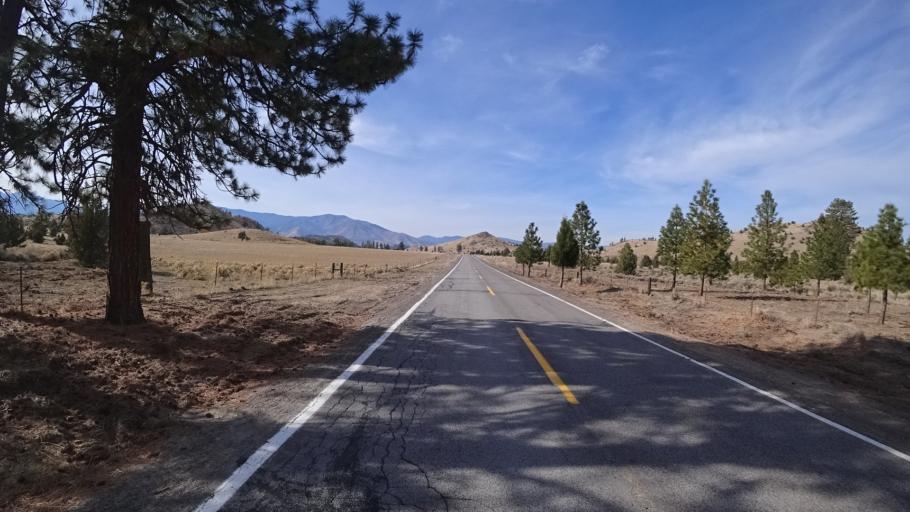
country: US
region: California
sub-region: Siskiyou County
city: Weed
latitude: 41.4940
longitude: -122.3853
